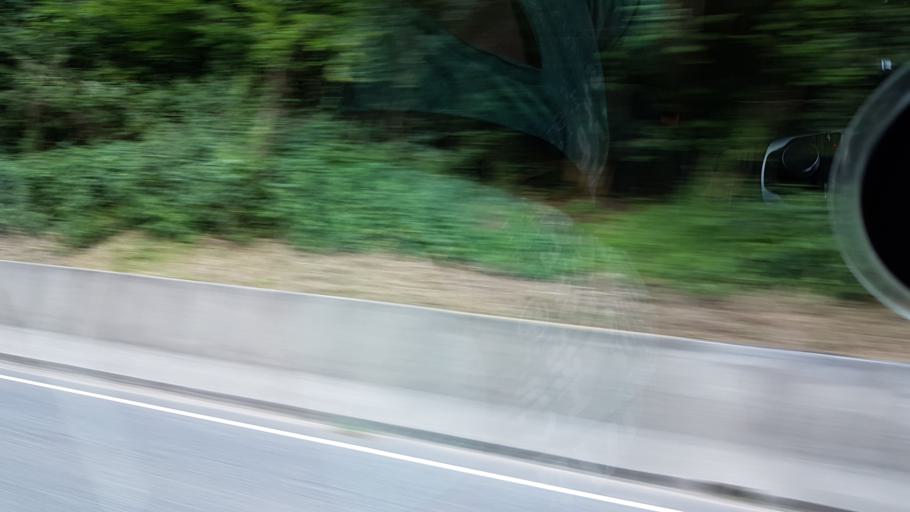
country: DE
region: Rheinland-Pfalz
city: Kalkofen
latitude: 49.7475
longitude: 7.8189
